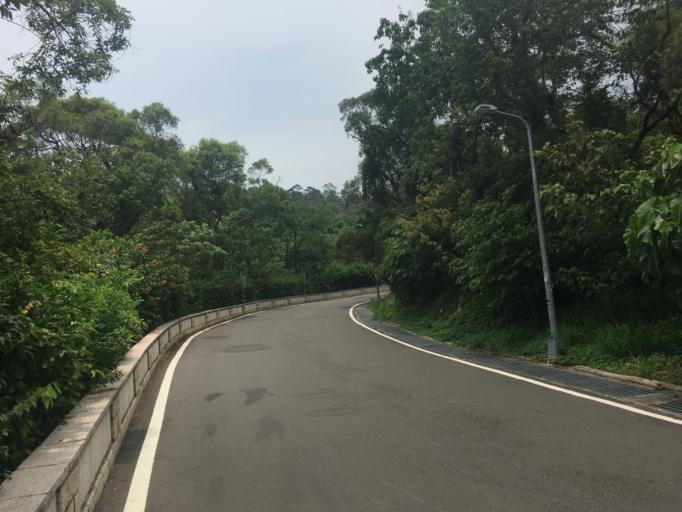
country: TW
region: Taipei
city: Taipei
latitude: 25.0895
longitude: 121.5518
